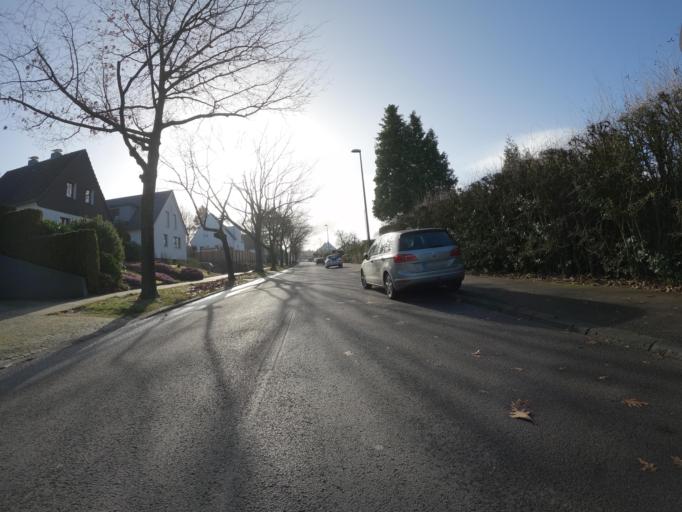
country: DE
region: North Rhine-Westphalia
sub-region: Regierungsbezirk Koln
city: Aachen
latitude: 50.7555
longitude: 6.1062
